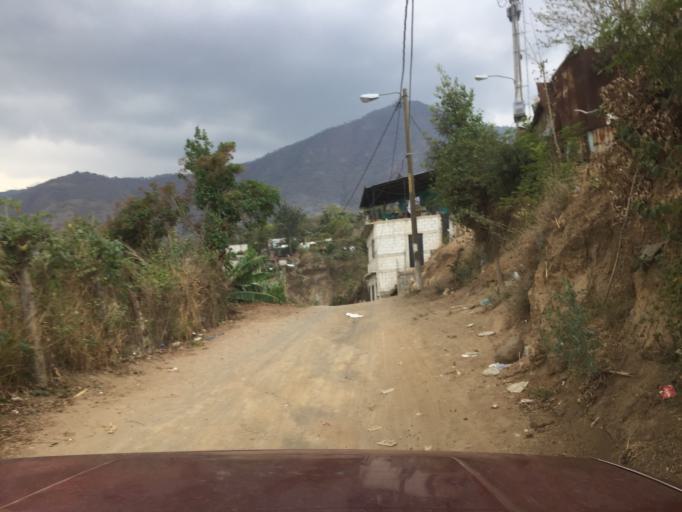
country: GT
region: Guatemala
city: Amatitlan
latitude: 14.4936
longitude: -90.6408
